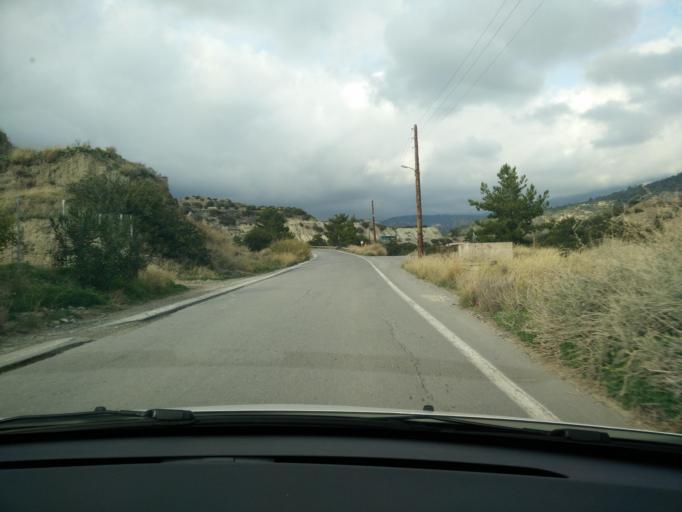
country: GR
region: Crete
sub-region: Nomos Lasithiou
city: Gra Liyia
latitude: 35.0139
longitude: 25.5835
